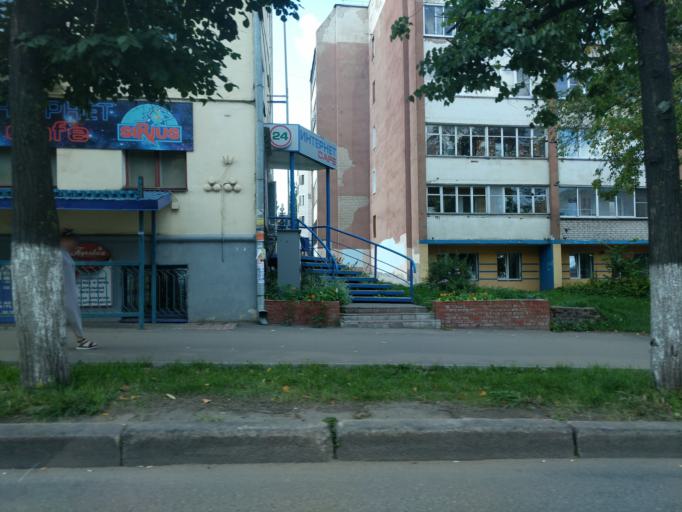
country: RU
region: Kirov
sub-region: Kirovo-Chepetskiy Rayon
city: Kirov
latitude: 58.6061
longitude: 49.6805
